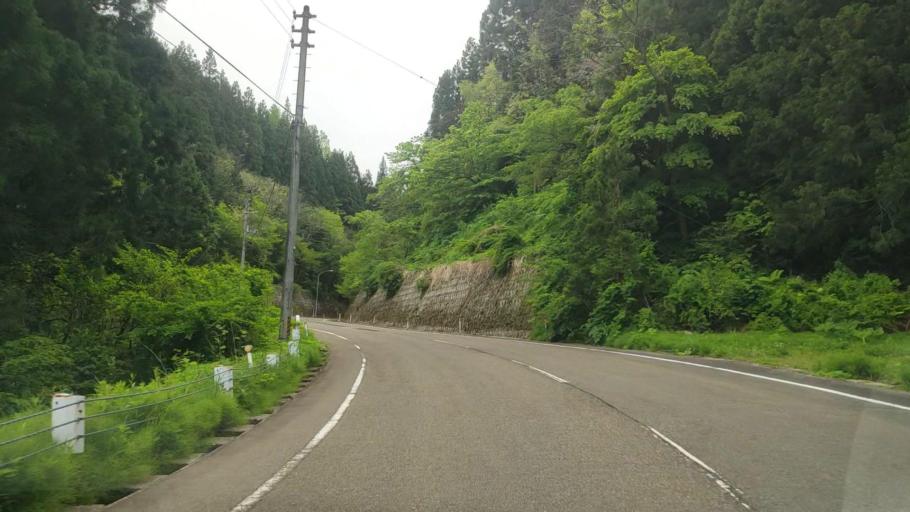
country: JP
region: Niigata
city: Gosen
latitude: 37.7144
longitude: 139.1122
